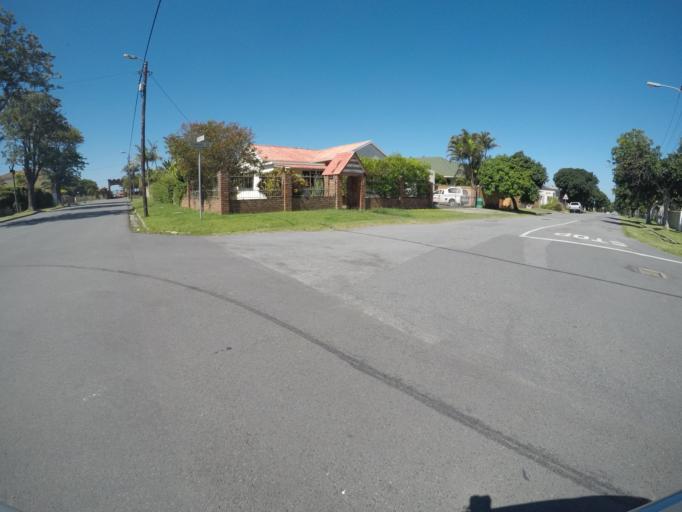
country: ZA
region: Eastern Cape
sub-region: Buffalo City Metropolitan Municipality
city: East London
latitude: -32.9852
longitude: 27.9294
